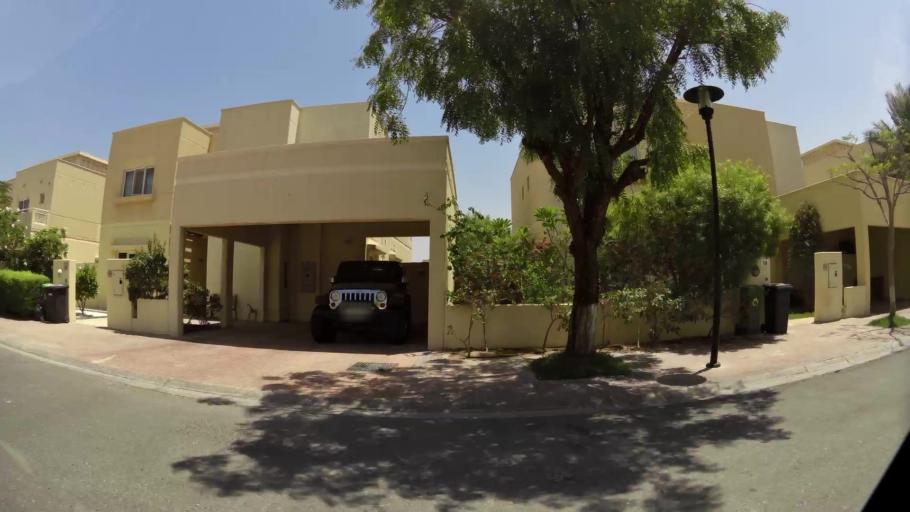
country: AE
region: Dubai
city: Dubai
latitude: 25.0430
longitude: 55.1709
